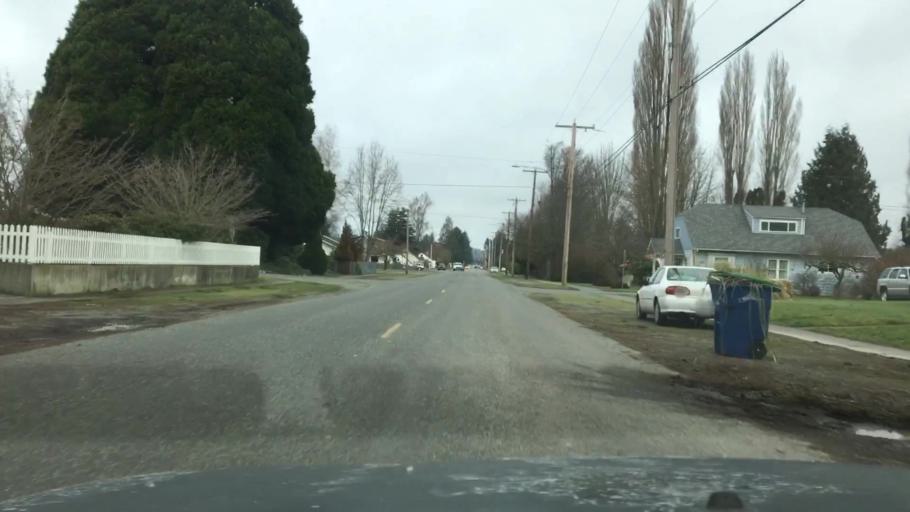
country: US
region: Washington
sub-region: Skagit County
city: Sedro-Woolley
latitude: 48.4948
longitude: -122.2260
